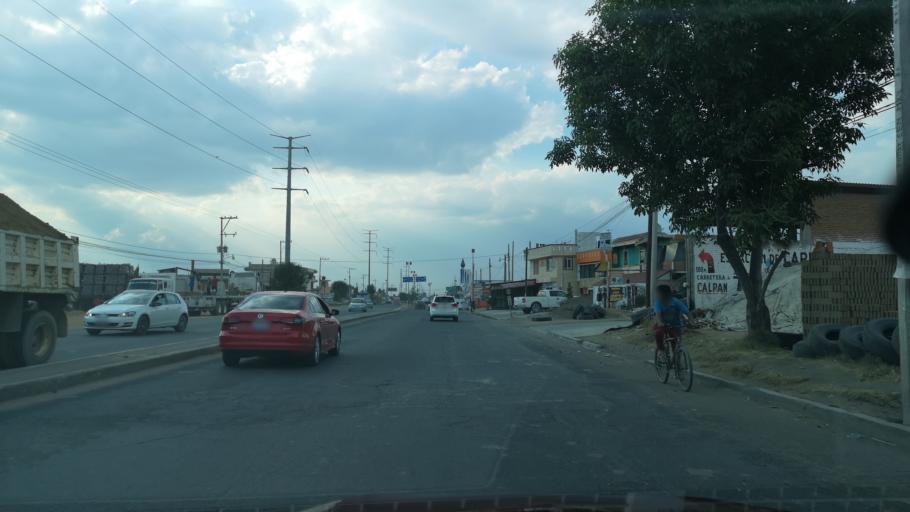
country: MX
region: Puebla
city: Cuanala
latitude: 19.0824
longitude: -98.3288
